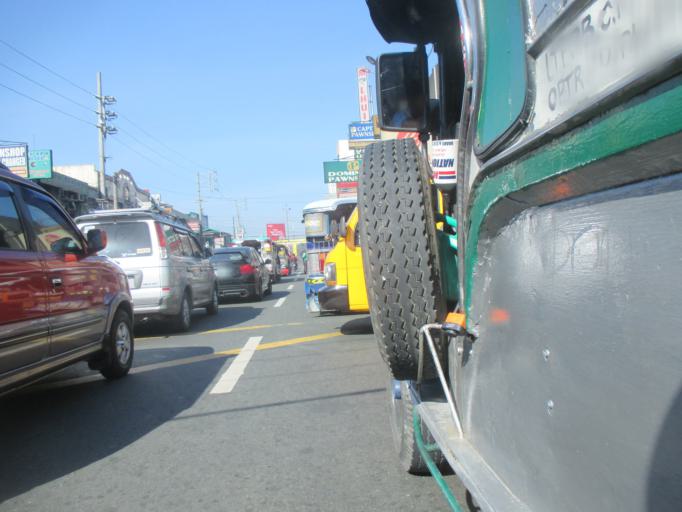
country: PH
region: Metro Manila
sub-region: Marikina
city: Calumpang
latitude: 14.6358
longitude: 121.0957
